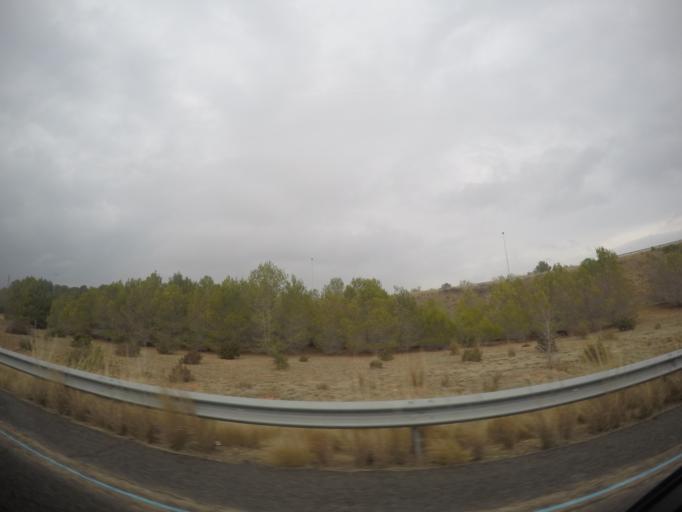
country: ES
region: Catalonia
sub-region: Provincia de Tarragona
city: Santa Oliva
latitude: 41.2694
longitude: 1.5481
